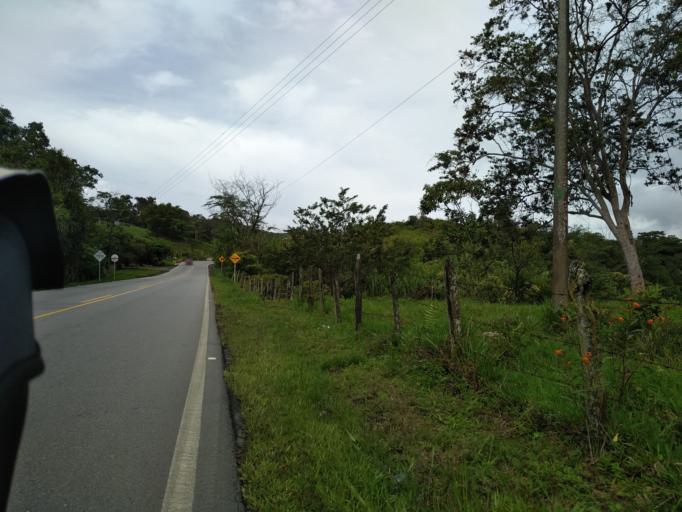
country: CO
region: Santander
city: Suaita
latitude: 6.0995
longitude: -73.3722
